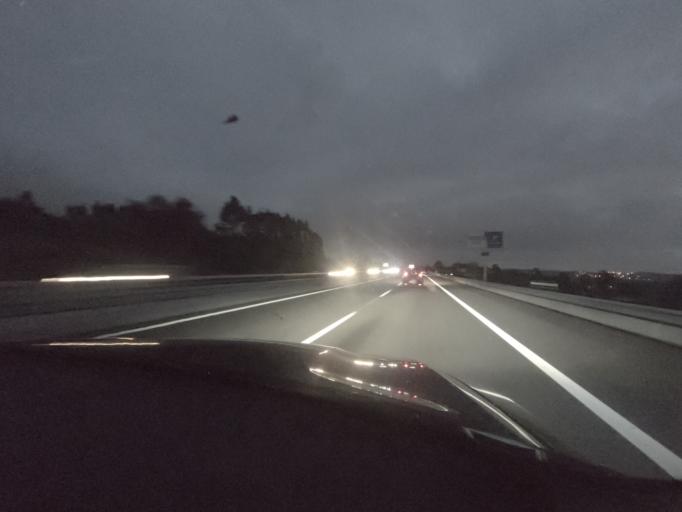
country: PT
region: Leiria
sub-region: Leiria
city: Caranguejeira
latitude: 39.7717
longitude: -8.7442
